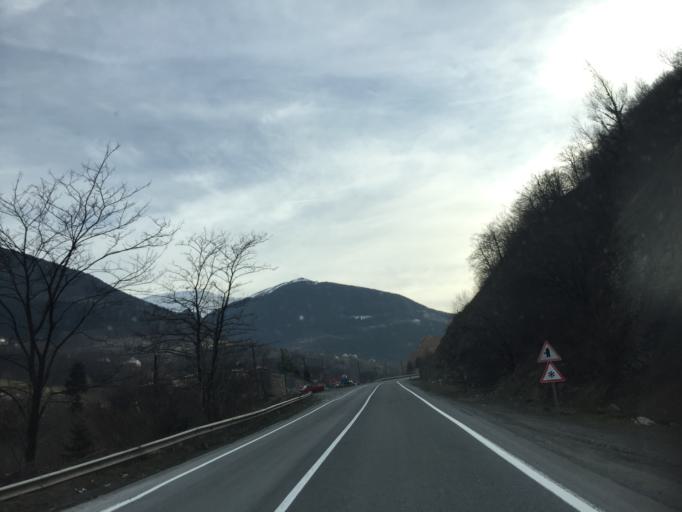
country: TR
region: Trabzon
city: Macka
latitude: 40.7214
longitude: 39.5184
